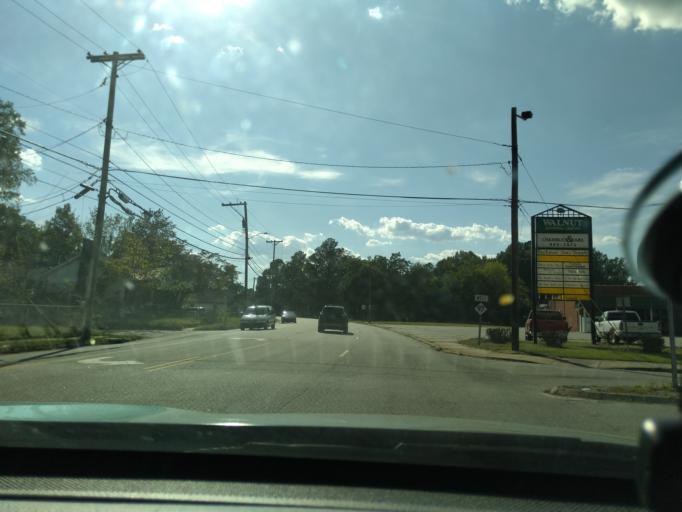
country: US
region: North Carolina
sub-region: Nash County
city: Rocky Mount
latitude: 35.9353
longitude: -77.8067
